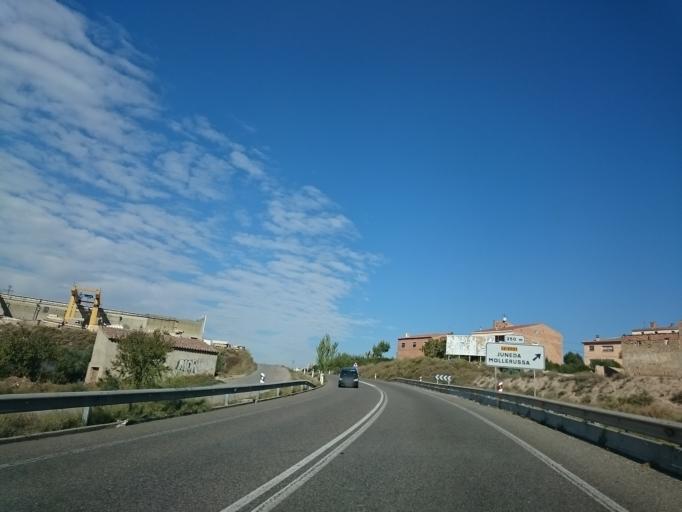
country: ES
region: Catalonia
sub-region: Provincia de Lleida
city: Juneda
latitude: 41.5505
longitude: 0.8205
